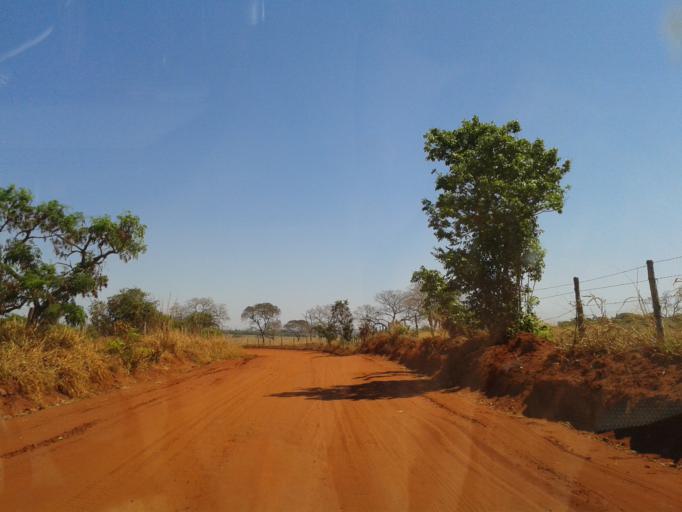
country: BR
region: Minas Gerais
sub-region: Ituiutaba
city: Ituiutaba
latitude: -18.9823
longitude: -49.3977
